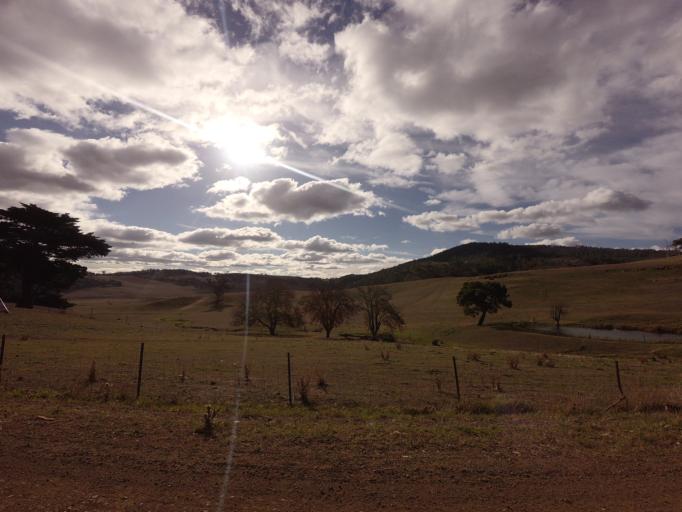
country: AU
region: Tasmania
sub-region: Brighton
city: Bridgewater
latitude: -42.4709
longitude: 147.2844
